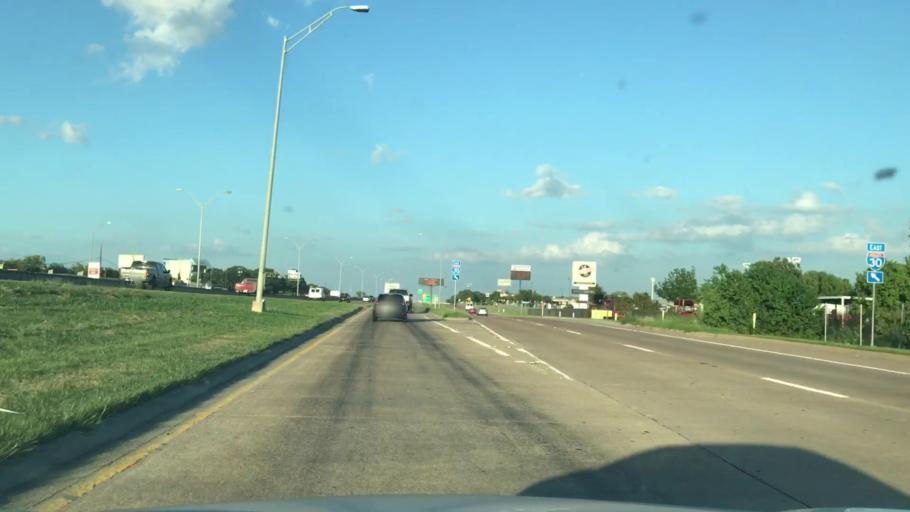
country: US
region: Texas
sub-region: Dallas County
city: Mesquite
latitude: 32.8044
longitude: -96.6663
